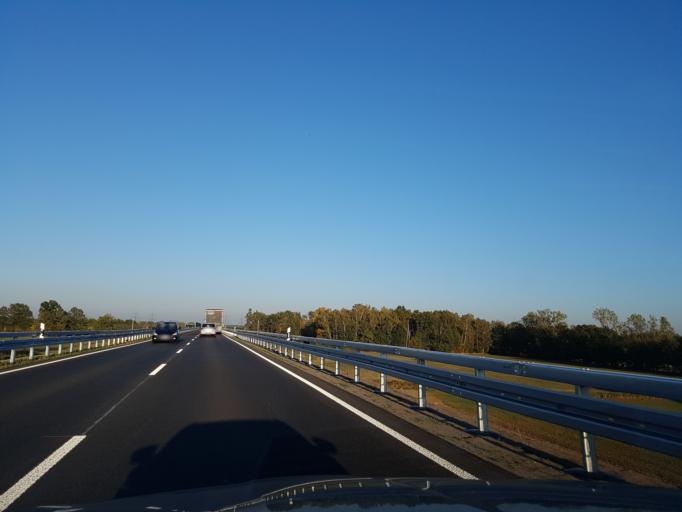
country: DE
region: Brandenburg
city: Bad Liebenwerda
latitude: 51.5050
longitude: 13.4080
